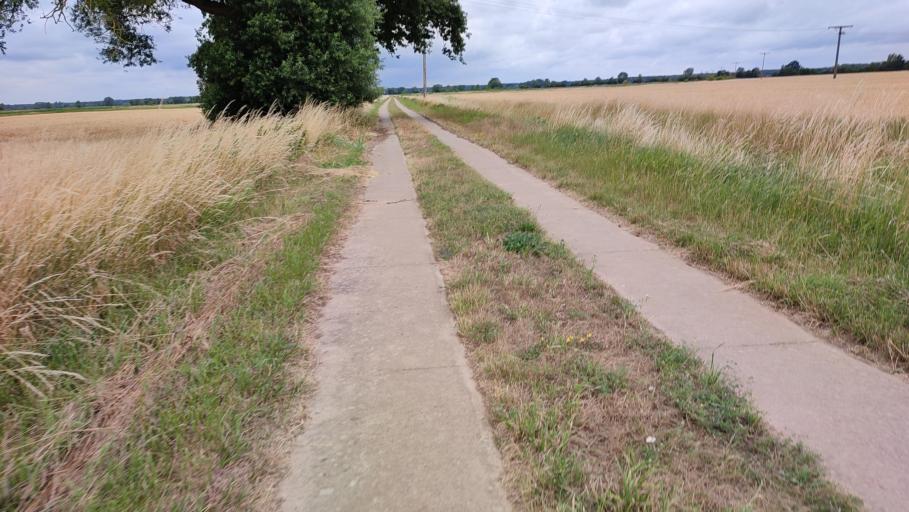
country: DE
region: Lower Saxony
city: Hitzacker
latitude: 53.1572
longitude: 11.1044
